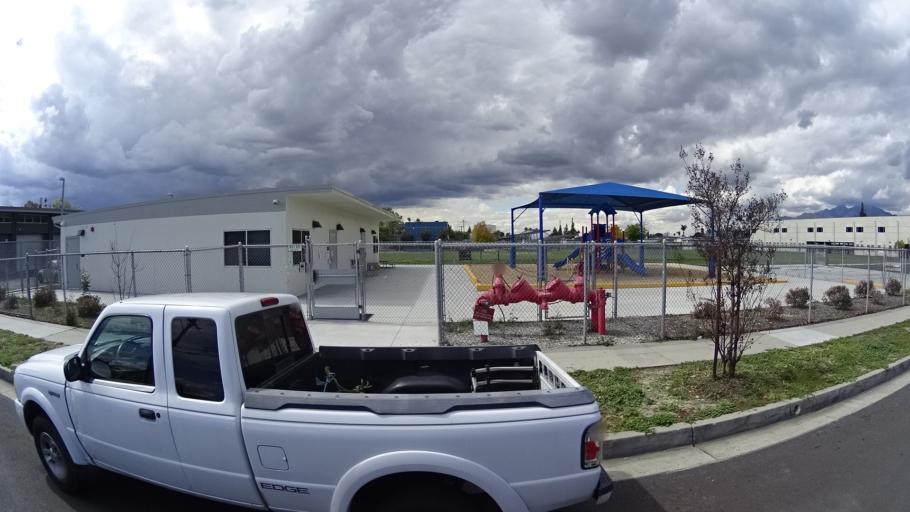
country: US
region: California
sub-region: Los Angeles County
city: Baldwin Park
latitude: 34.0959
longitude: -117.9555
